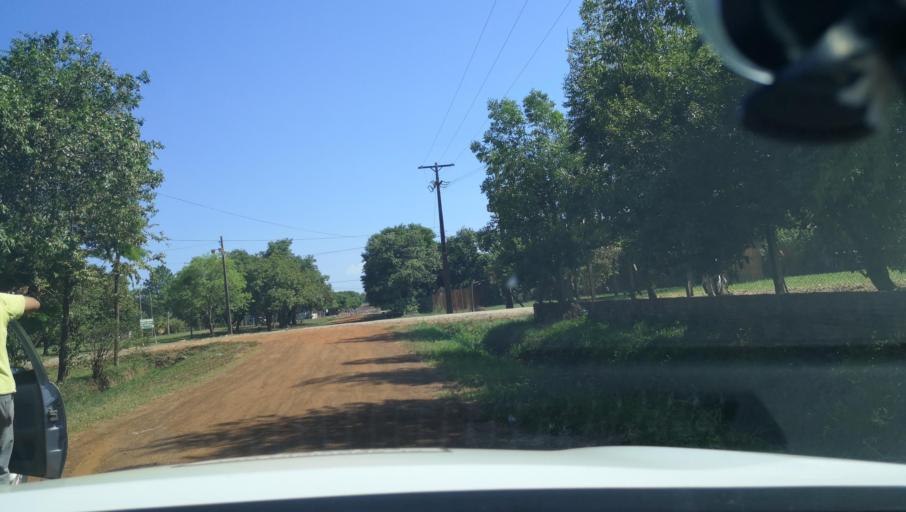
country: PY
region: Itapua
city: Carmen del Parana
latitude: -27.1685
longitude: -56.2310
